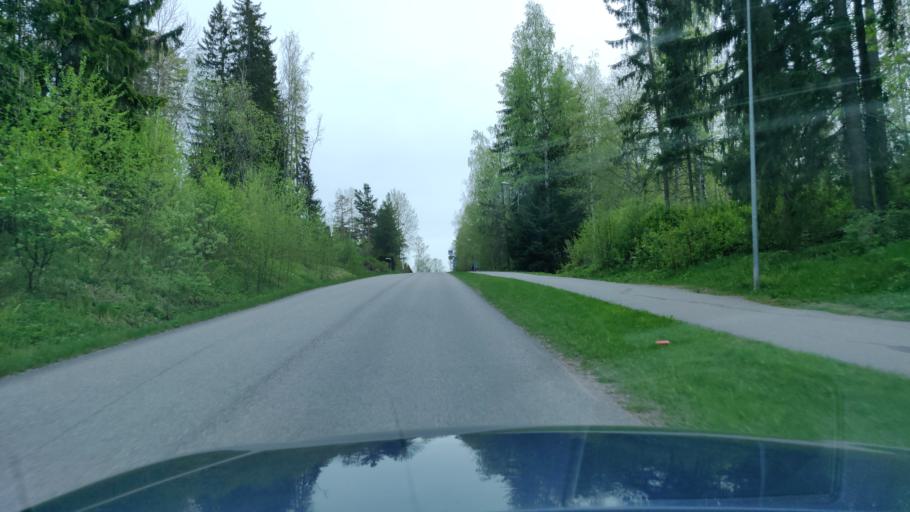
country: FI
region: Uusimaa
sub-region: Helsinki
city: Nurmijaervi
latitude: 60.3733
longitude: 24.7544
